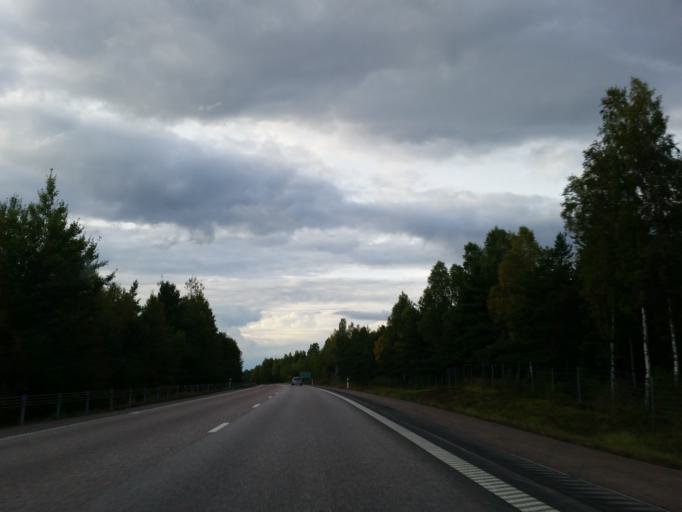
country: SE
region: Stockholm
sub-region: Sigtuna Kommun
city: Marsta
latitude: 59.6967
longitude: 17.8650
